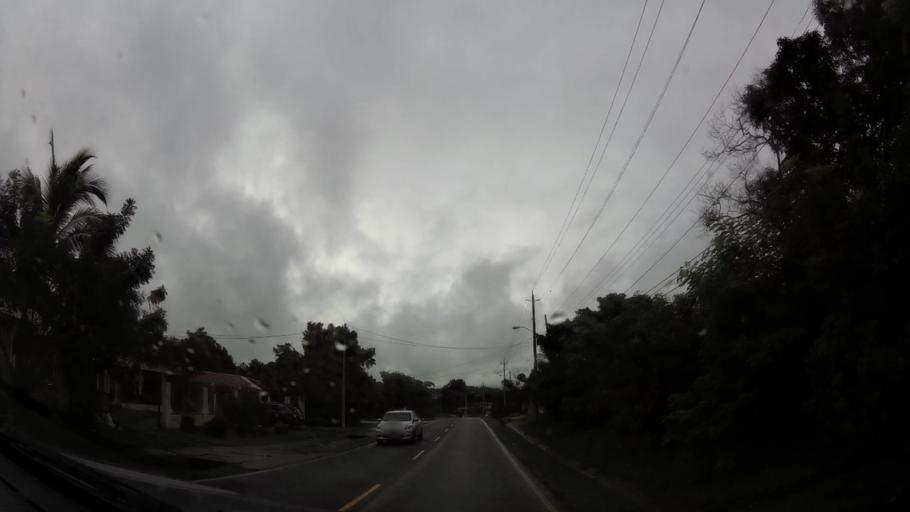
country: PA
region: Veraguas
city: Santiago de Veraguas
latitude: 8.0943
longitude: -80.9609
